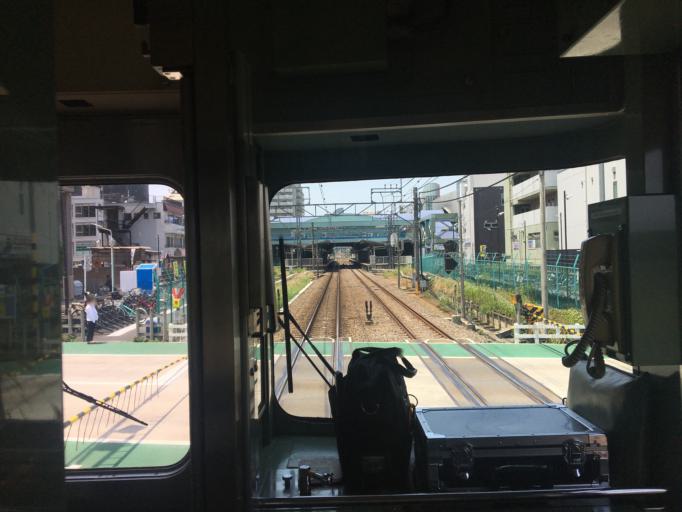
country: JP
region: Tokyo
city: Tanashicho
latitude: 35.7593
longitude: 139.5351
